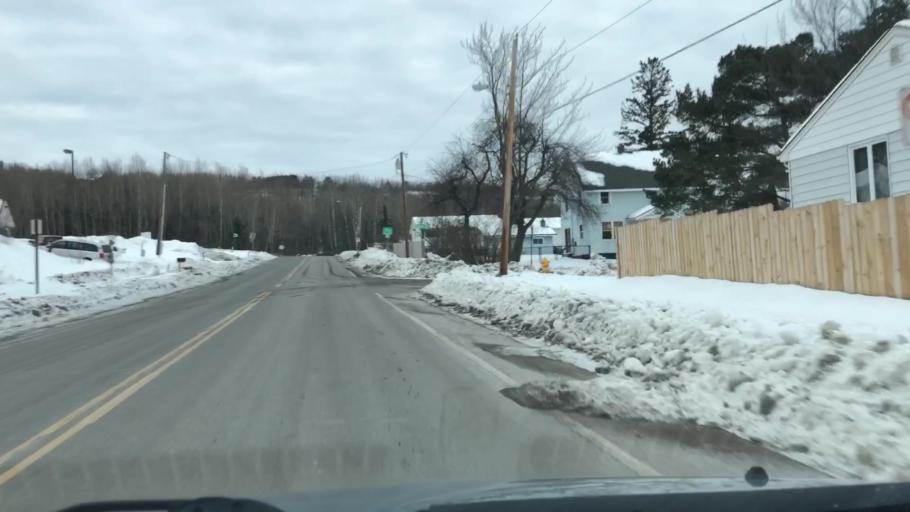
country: US
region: Minnesota
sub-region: Saint Louis County
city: Arnold
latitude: 46.8390
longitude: -92.0371
